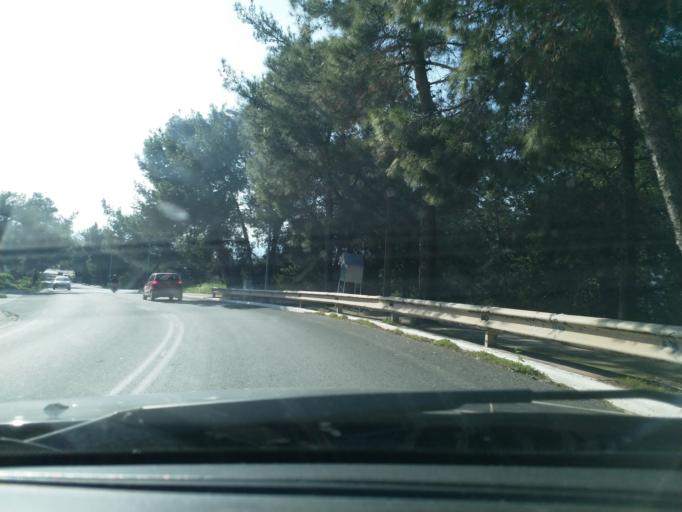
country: GR
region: Crete
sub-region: Nomos Chanias
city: Chania
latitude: 35.5209
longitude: 24.0554
